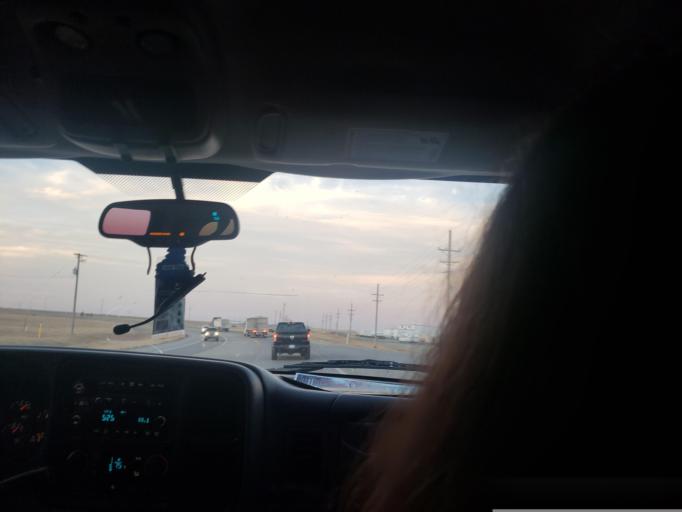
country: US
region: Kansas
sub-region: Seward County
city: Liberal
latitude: 37.0649
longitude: -100.9045
